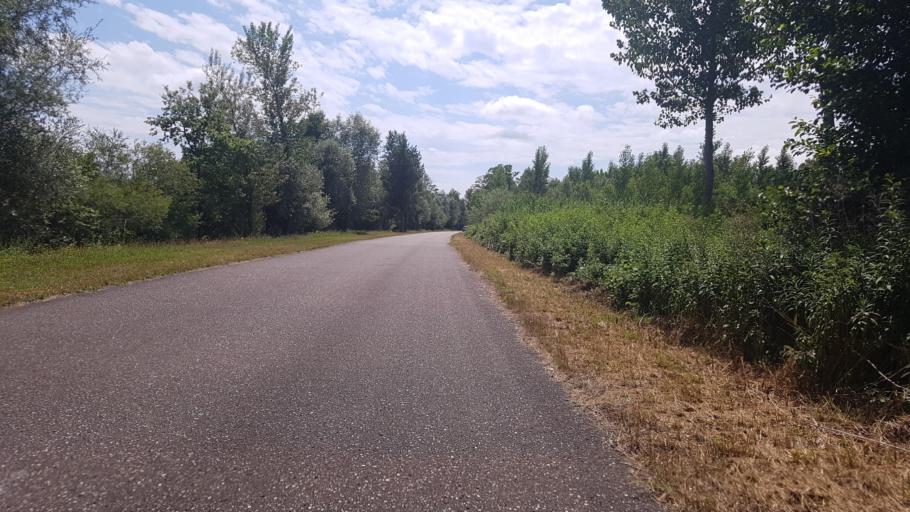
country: DE
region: Baden-Wuerttemberg
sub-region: Karlsruhe Region
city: Rheinmuenster
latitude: 48.7684
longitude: 8.0200
